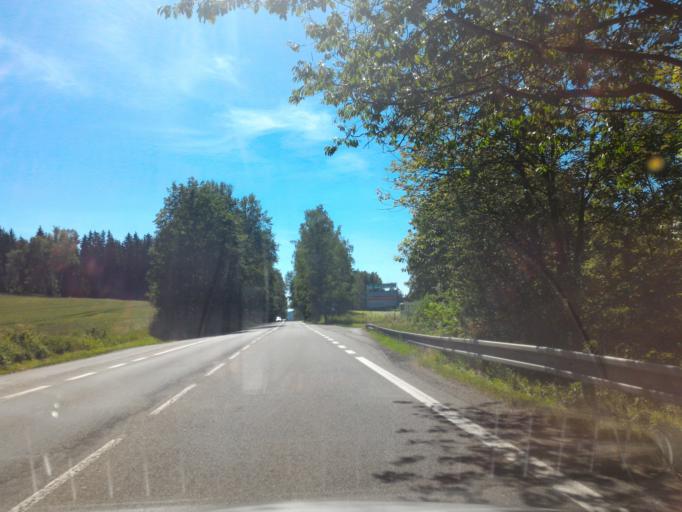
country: CZ
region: Vysocina
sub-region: Okres Jihlava
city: Jihlava
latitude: 49.3842
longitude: 15.5229
